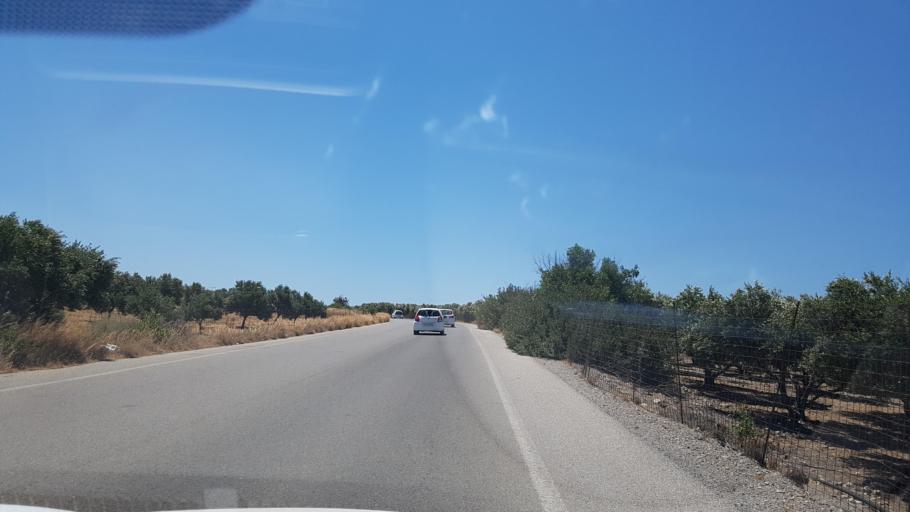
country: GR
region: Crete
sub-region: Nomos Chanias
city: Vryses
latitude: 35.3034
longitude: 23.5376
